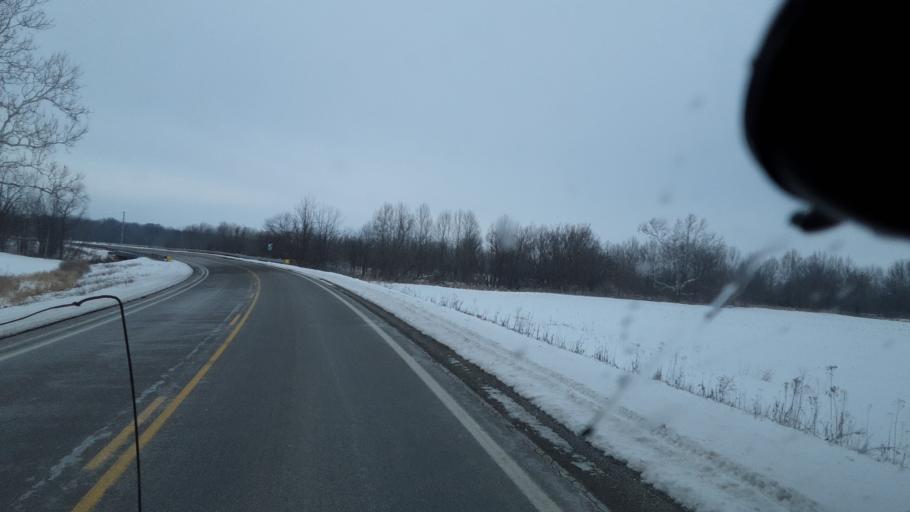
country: US
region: Ohio
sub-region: Champaign County
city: Mechanicsburg
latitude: 40.1219
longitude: -83.4538
